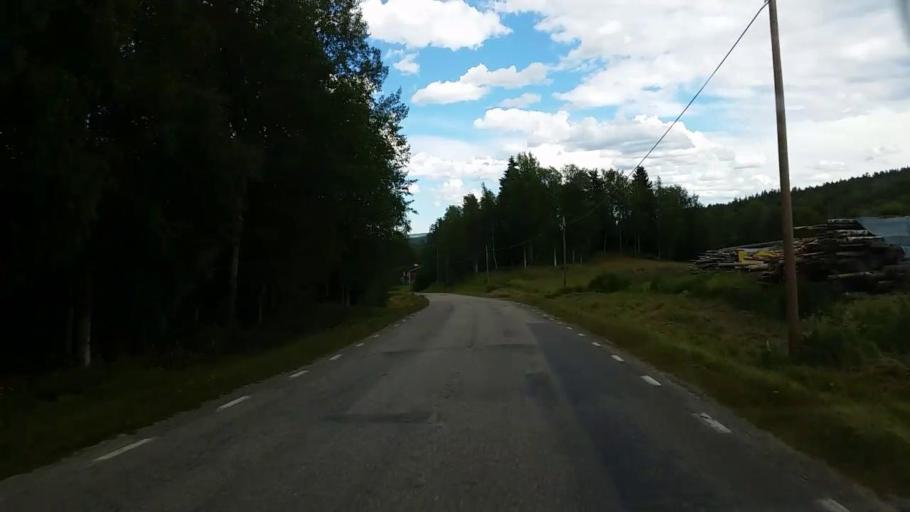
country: SE
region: Gaevleborg
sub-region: Ljusdals Kommun
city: Jaervsoe
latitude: 61.6671
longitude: 16.0848
